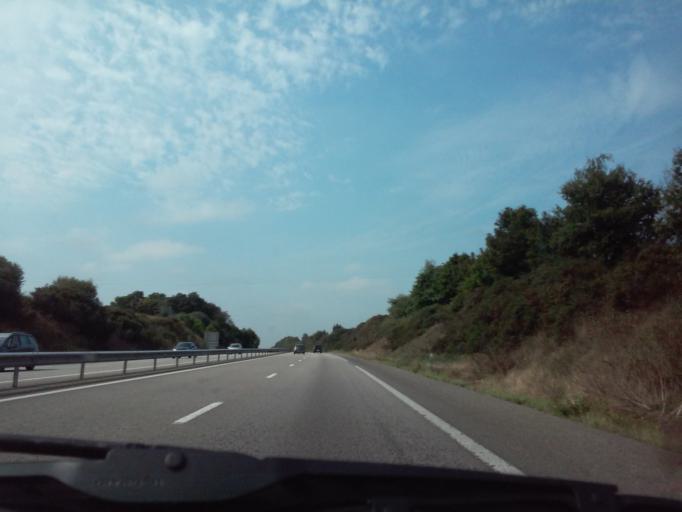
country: FR
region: Brittany
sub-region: Departement du Morbihan
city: Campeneac
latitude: 47.9350
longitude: -2.3113
